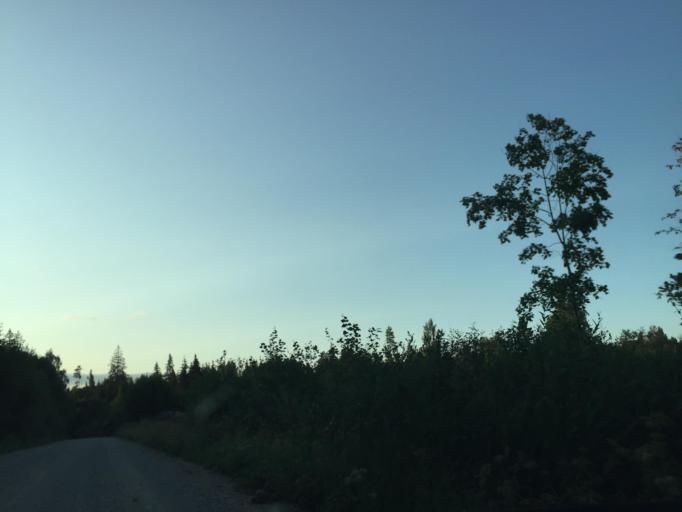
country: LV
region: Kuldigas Rajons
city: Kuldiga
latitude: 57.1216
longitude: 22.2097
